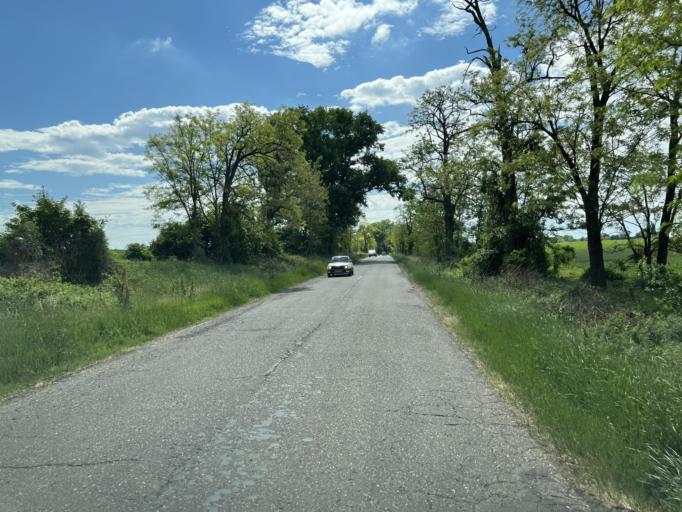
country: HU
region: Pest
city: Vacszentlaszlo
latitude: 47.5559
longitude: 19.5707
